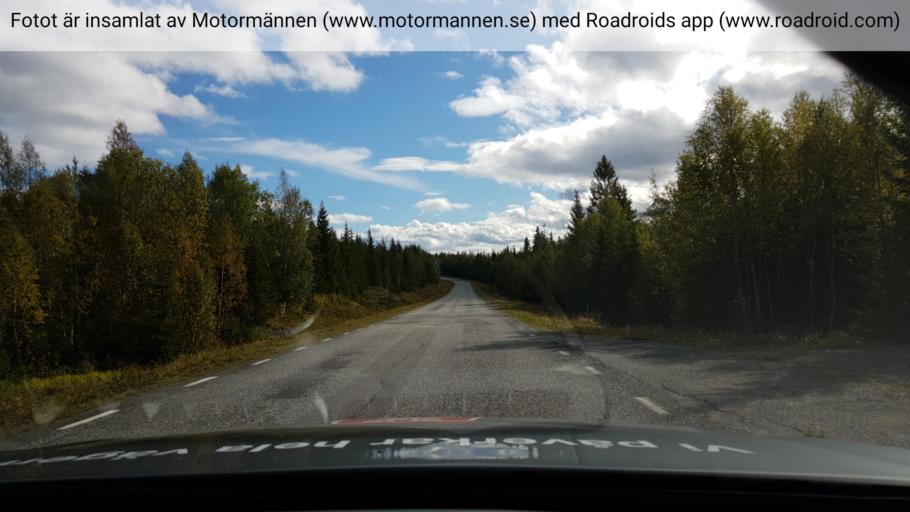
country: SE
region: Jaemtland
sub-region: Are Kommun
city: Are
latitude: 63.7373
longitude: 13.0522
